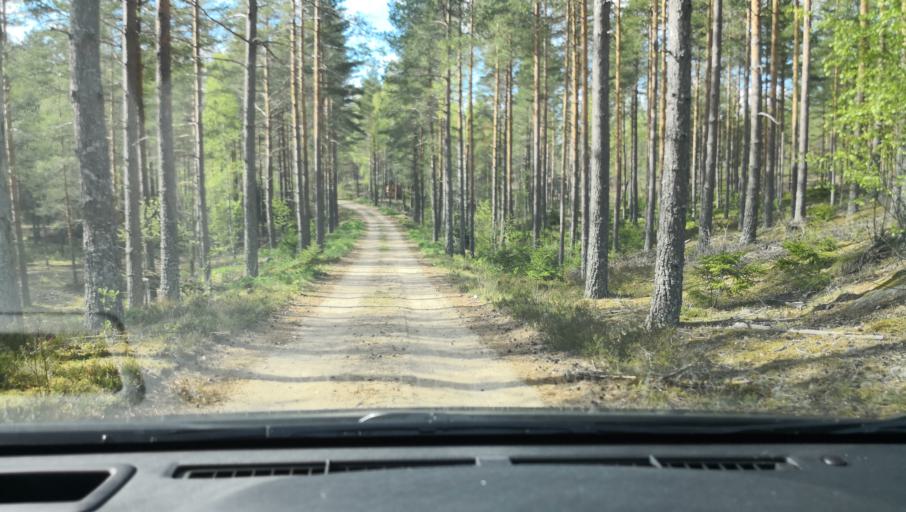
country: SE
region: OErebro
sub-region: Askersunds Kommun
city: Asbro
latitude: 59.0261
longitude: 15.0483
